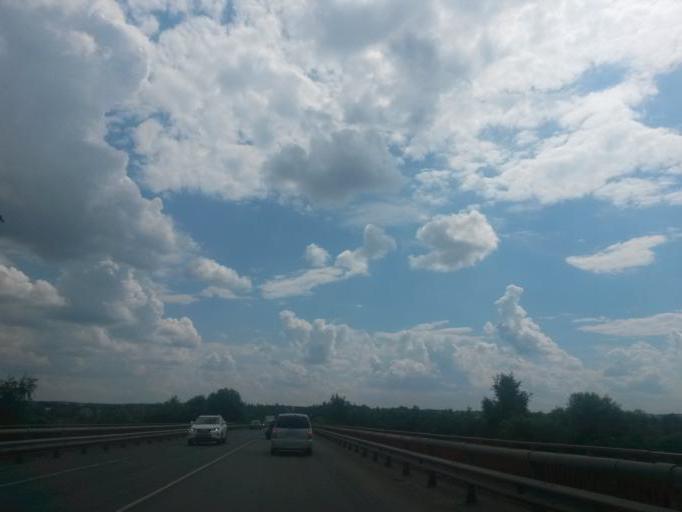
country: RU
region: Moskovskaya
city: Gorki-Leninskiye
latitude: 55.4895
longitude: 37.7804
